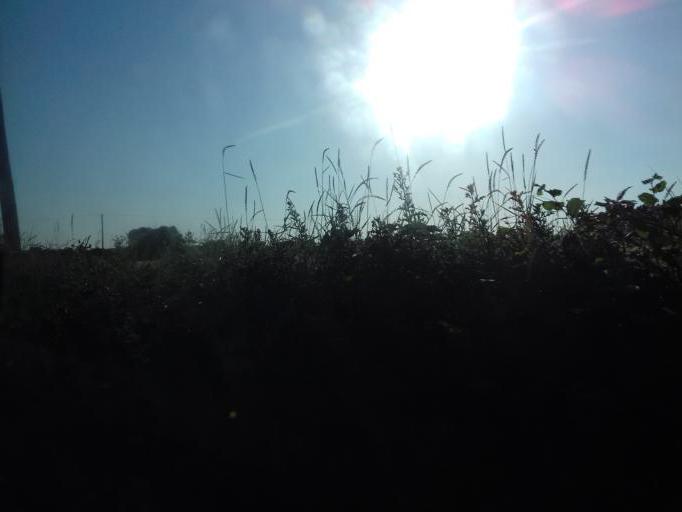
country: IE
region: Leinster
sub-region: Fingal County
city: Blanchardstown
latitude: 53.4352
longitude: -6.3575
